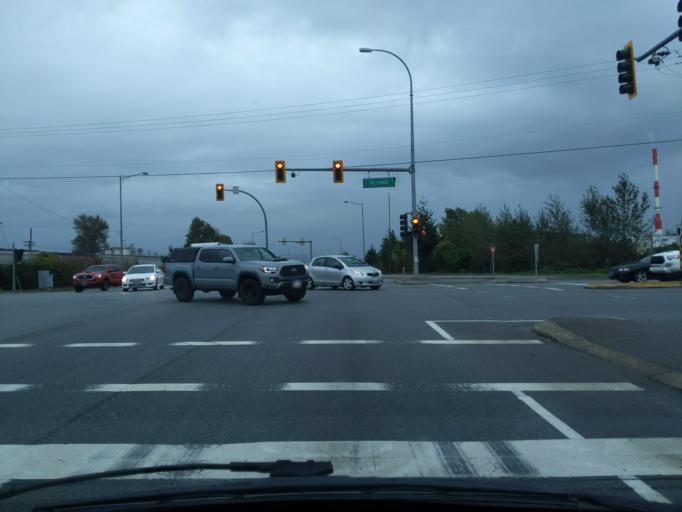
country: CA
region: British Columbia
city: Pitt Meadows
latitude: 49.1809
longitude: -122.6906
